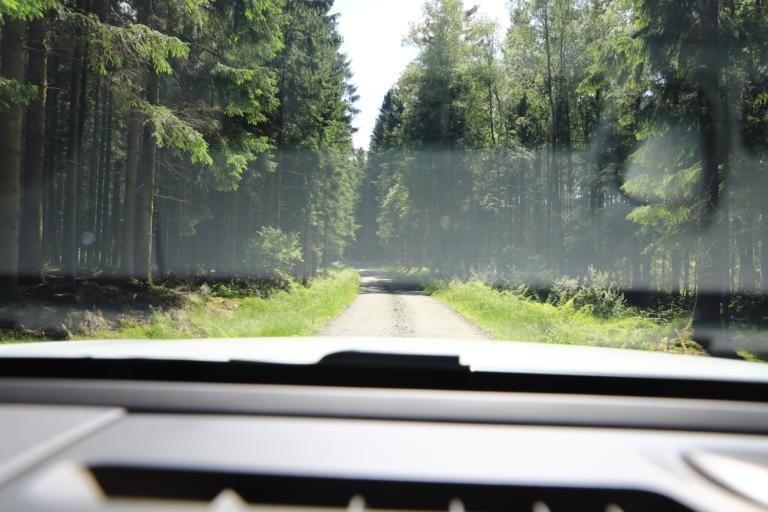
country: SE
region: Halland
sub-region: Varbergs Kommun
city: Tvaaker
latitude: 57.0986
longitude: 12.4820
